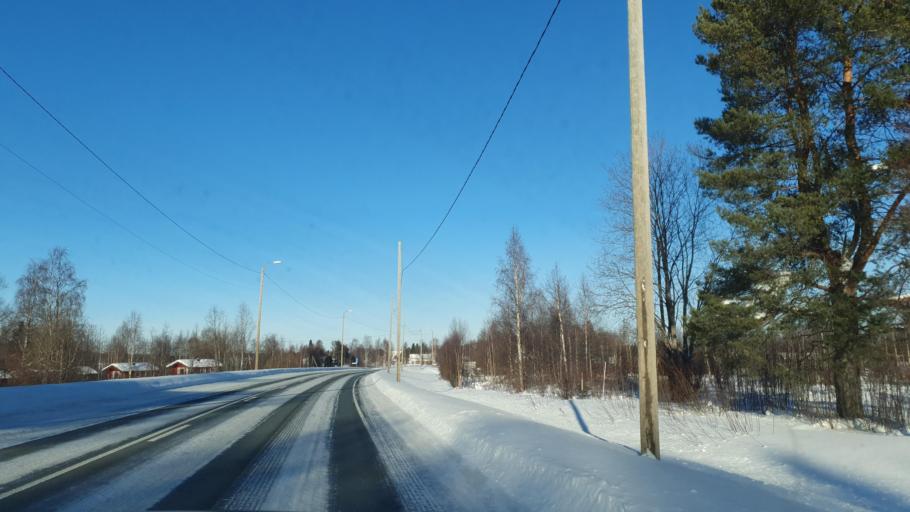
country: FI
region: Lapland
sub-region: Torniolaakso
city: Pello
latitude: 66.6345
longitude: 23.8767
